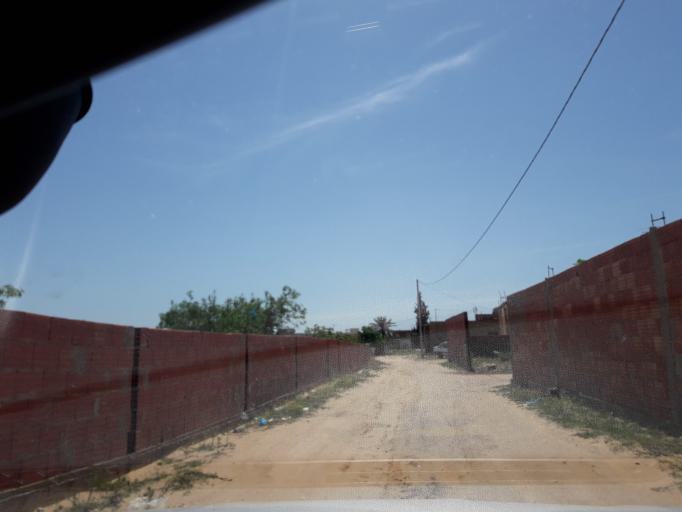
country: TN
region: Safaqis
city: Sfax
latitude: 34.7455
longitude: 10.5120
